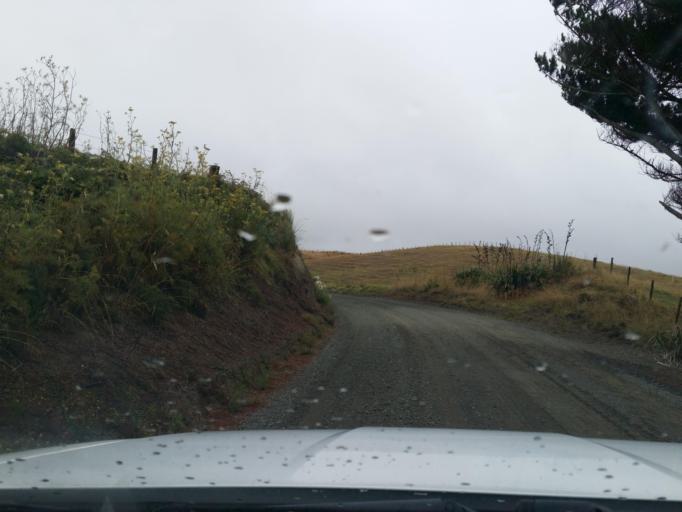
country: NZ
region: Northland
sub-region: Kaipara District
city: Dargaville
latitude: -36.0579
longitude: 173.8678
